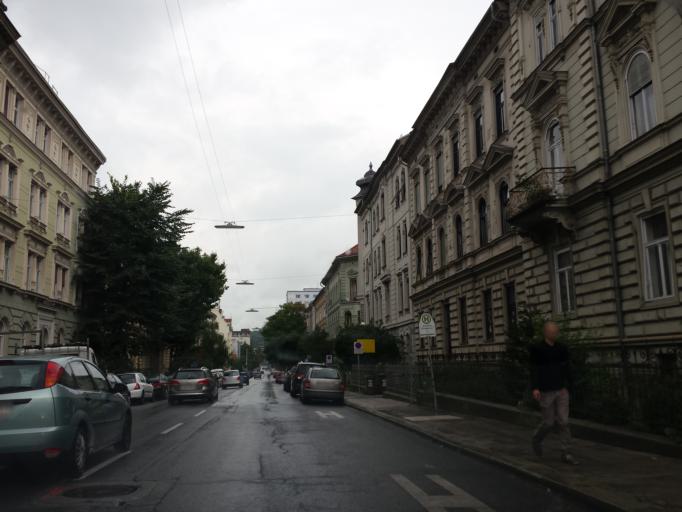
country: AT
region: Styria
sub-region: Graz Stadt
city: Graz
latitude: 47.0798
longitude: 15.4420
